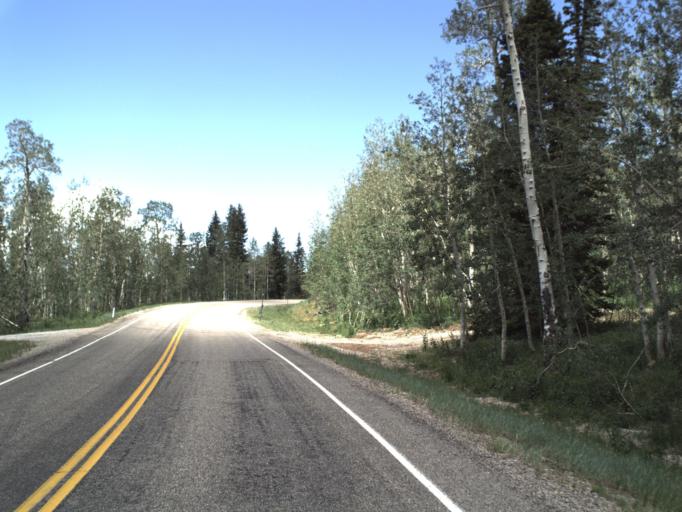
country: US
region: Utah
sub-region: Weber County
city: Wolf Creek
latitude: 41.4657
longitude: -111.4944
